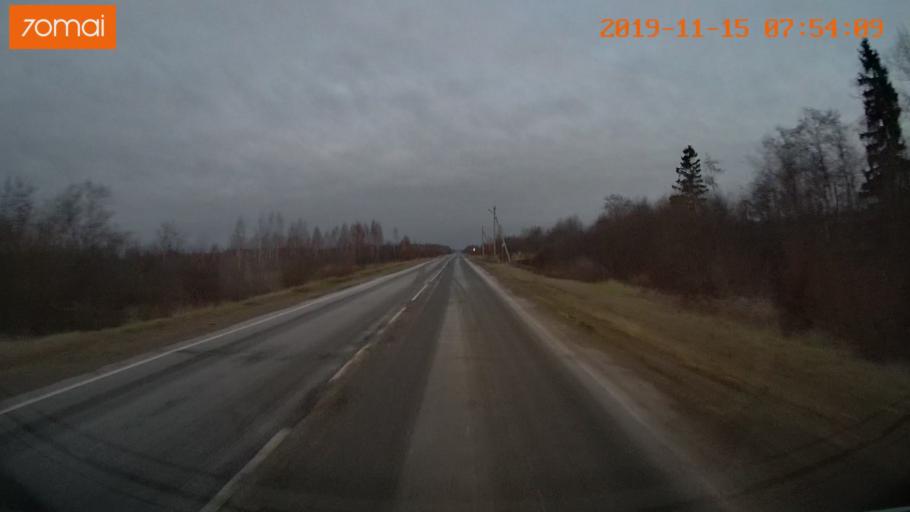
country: RU
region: Vologda
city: Cherepovets
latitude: 58.8958
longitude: 38.1792
